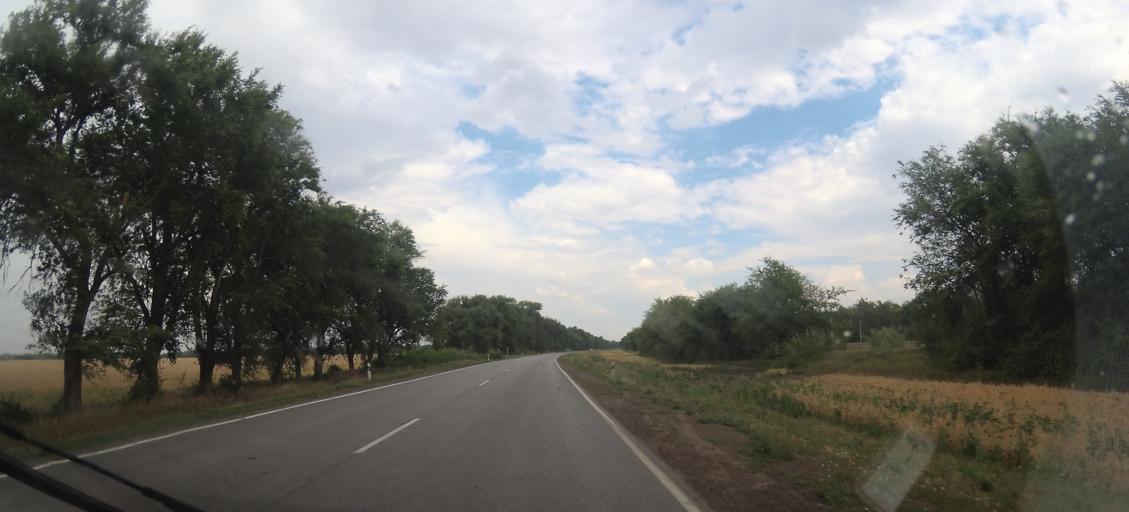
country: RU
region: Rostov
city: Peschanokopskoye
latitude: 46.2037
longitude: 41.2012
